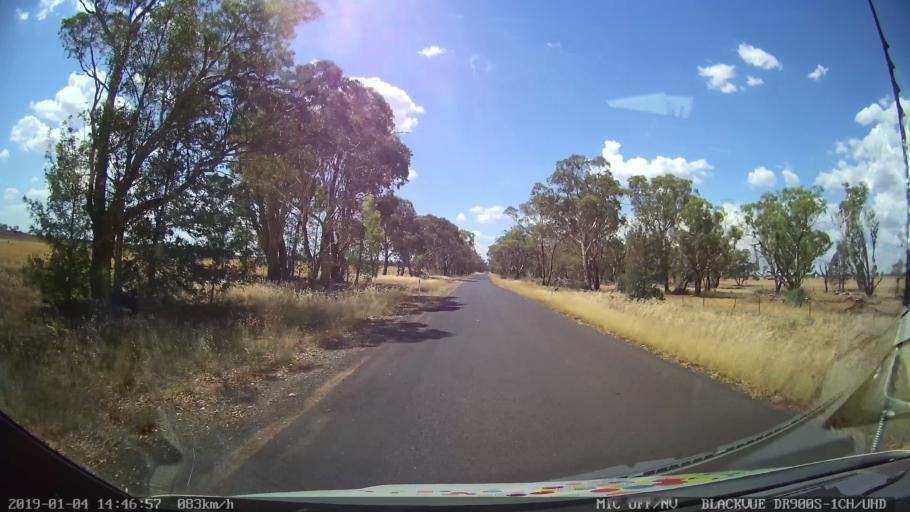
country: AU
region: New South Wales
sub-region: Dubbo Municipality
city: Dubbo
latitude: -32.0752
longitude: 148.6593
